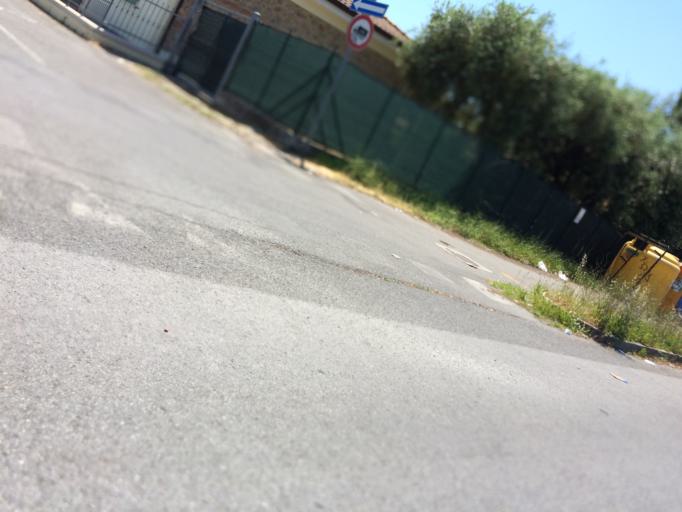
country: IT
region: Tuscany
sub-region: Provincia di Massa-Carrara
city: Massa
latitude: 44.0402
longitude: 10.1287
